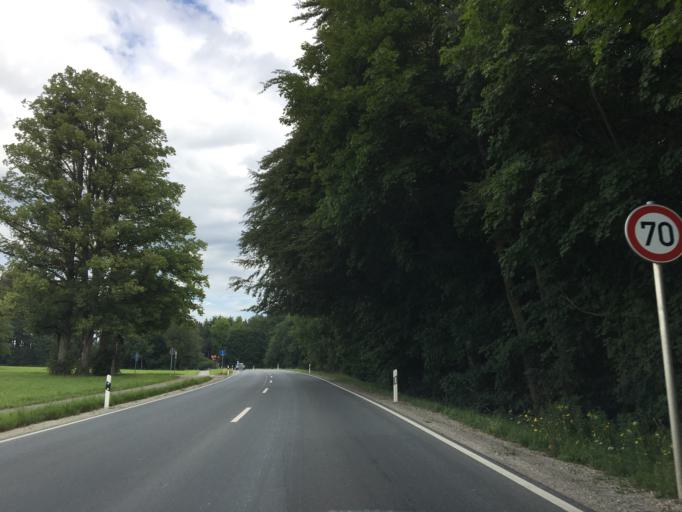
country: DE
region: Bavaria
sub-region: Upper Bavaria
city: Otterfing
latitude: 47.8896
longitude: 11.6843
